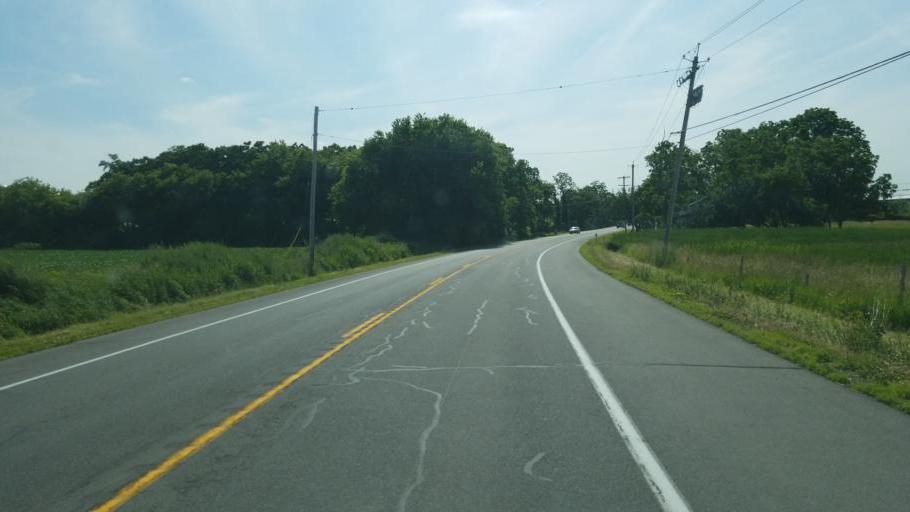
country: US
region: New York
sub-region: Livingston County
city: Lima
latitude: 42.9083
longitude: -77.5899
